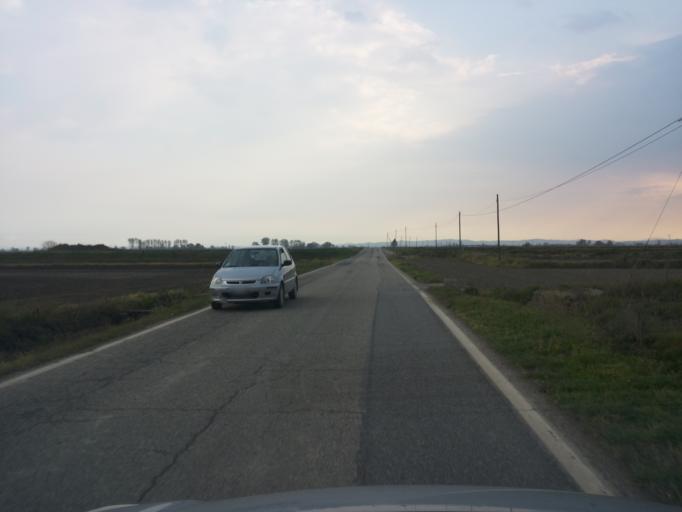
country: IT
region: Piedmont
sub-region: Provincia di Vercelli
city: Caresana
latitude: 45.2134
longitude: 8.5042
